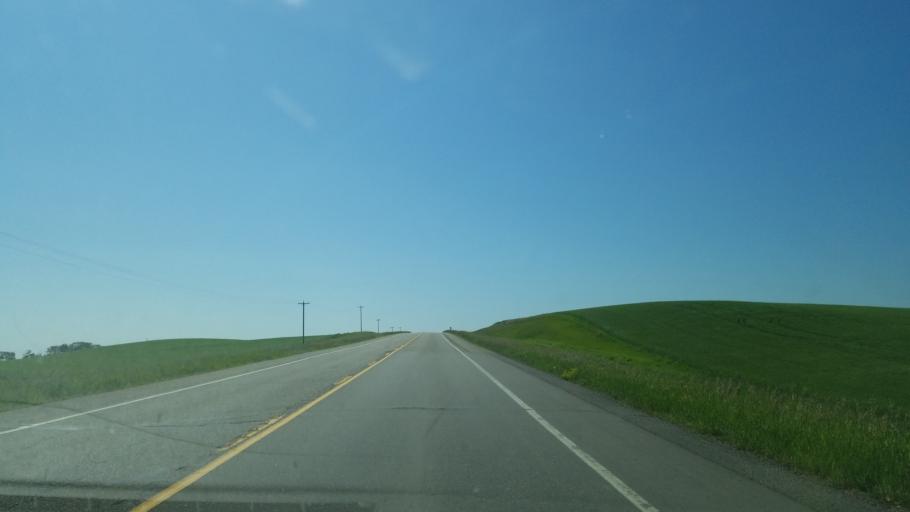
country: CA
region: Alberta
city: Provost
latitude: 52.3613
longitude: -110.1559
